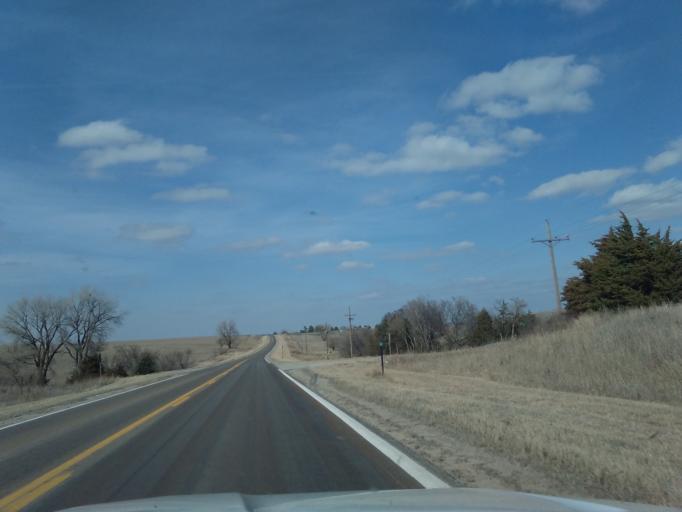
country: US
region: Nebraska
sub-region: Jefferson County
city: Fairbury
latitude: 40.0733
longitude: -96.9352
